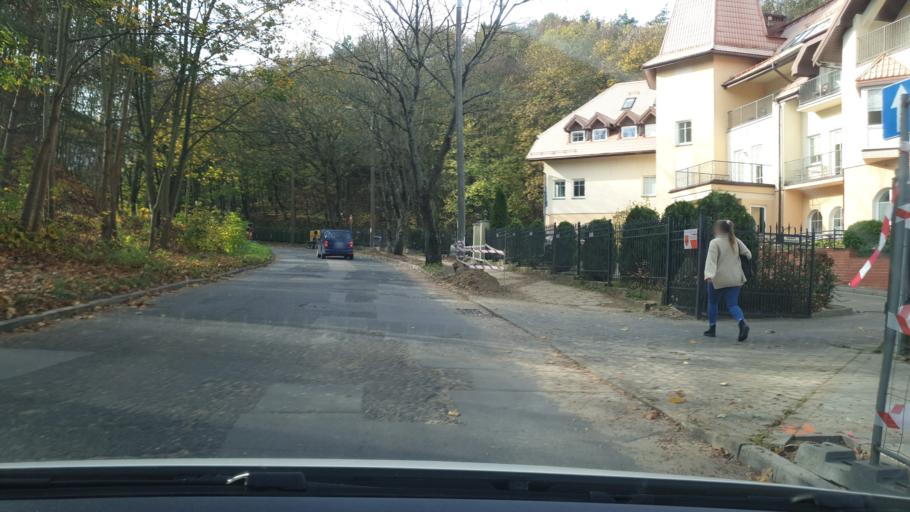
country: PL
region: Pomeranian Voivodeship
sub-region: Powiat gdanski
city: Kowale
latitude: 54.3628
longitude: 18.5874
